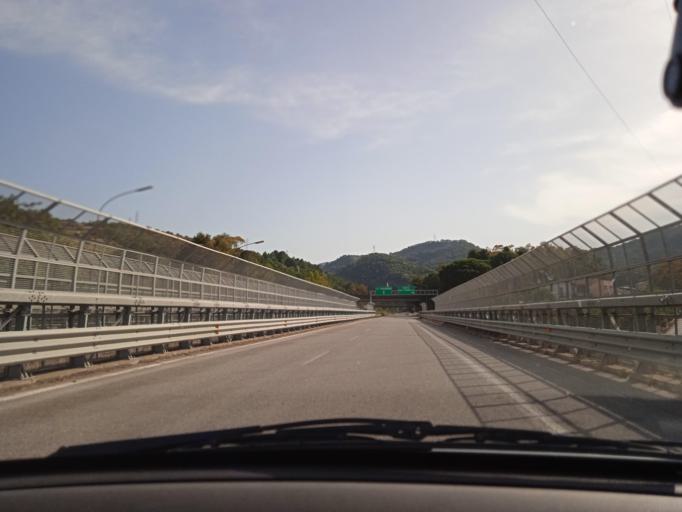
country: IT
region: Sicily
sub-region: Messina
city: Brolo
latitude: 38.1501
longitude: 14.8311
